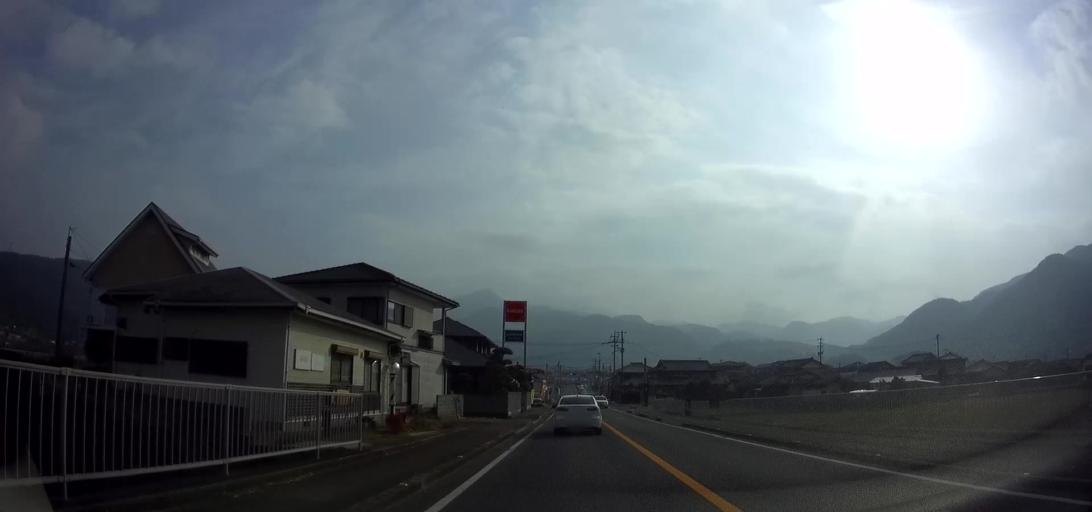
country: JP
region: Nagasaki
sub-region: Isahaya-shi
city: Isahaya
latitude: 32.7882
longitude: 130.1912
